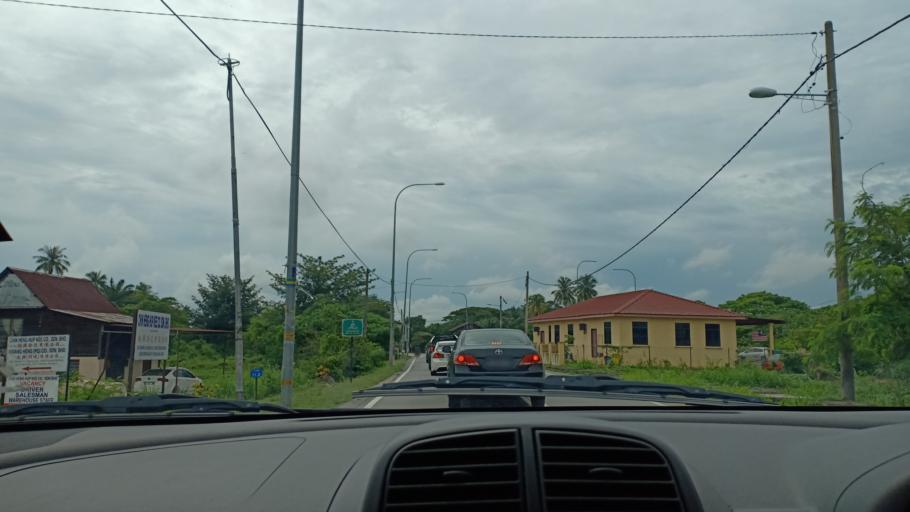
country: MY
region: Penang
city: Bukit Mertajam
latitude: 5.4084
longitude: 100.4828
